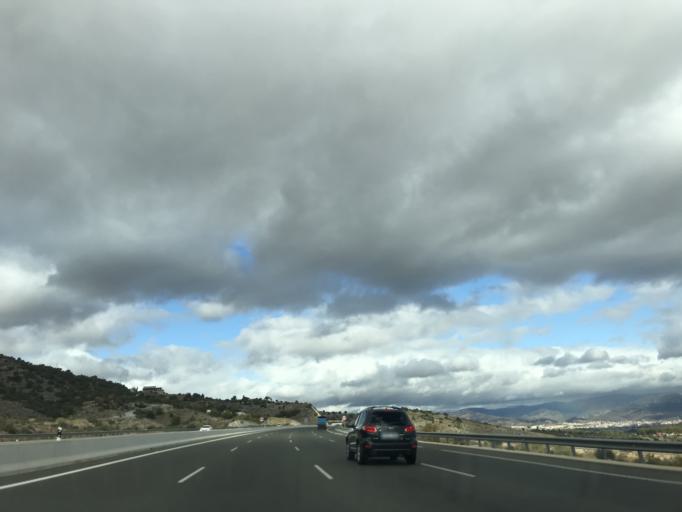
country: ES
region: Andalusia
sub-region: Provincia de Malaga
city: Torremolinos
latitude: 36.6395
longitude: -4.5143
